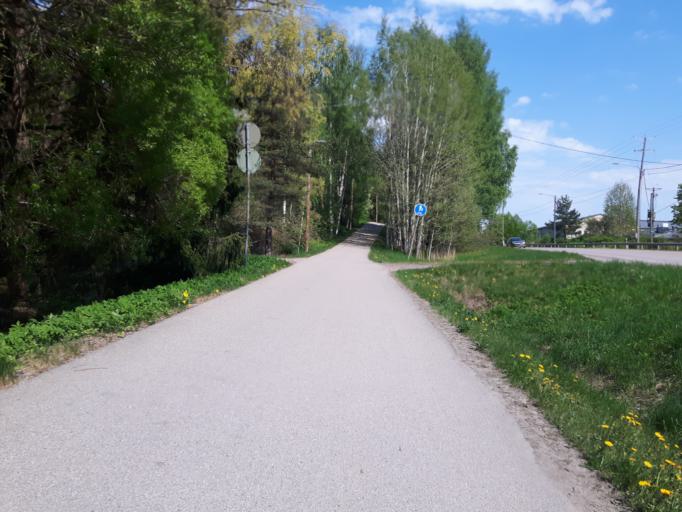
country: FI
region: Uusimaa
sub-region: Porvoo
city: Porvoo
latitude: 60.3798
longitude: 25.6159
